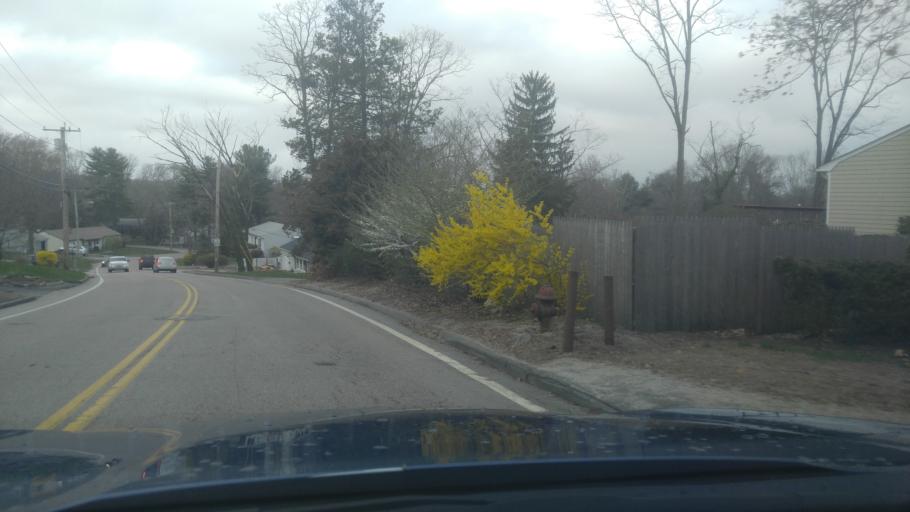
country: US
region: Rhode Island
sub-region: Kent County
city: East Greenwich
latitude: 41.6938
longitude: -71.4695
